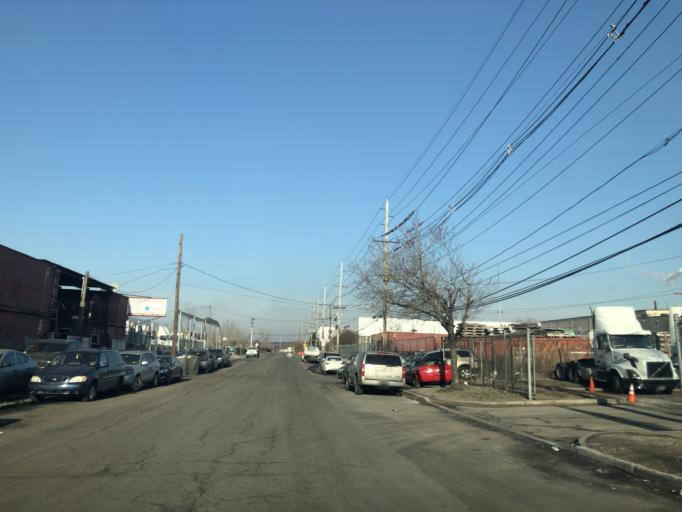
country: US
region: New Jersey
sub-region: Hudson County
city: Harrison
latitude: 40.7188
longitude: -74.1325
